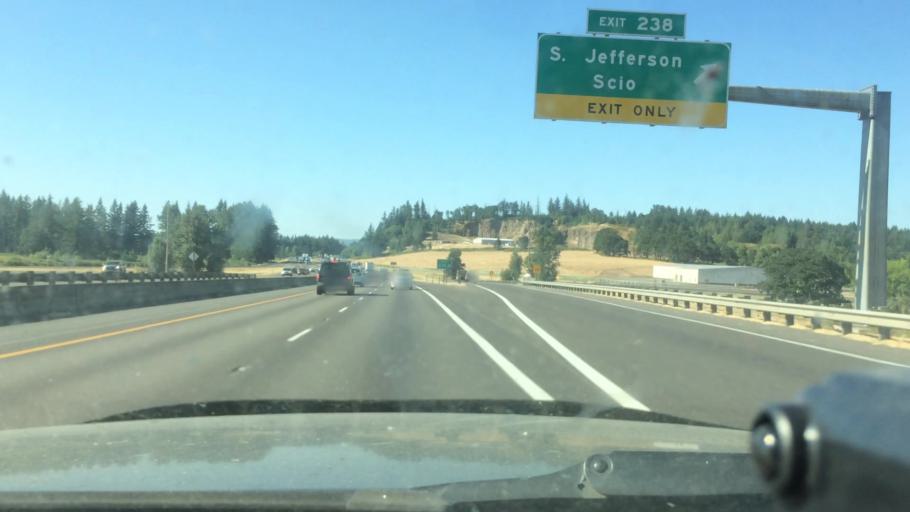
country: US
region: Oregon
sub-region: Linn County
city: Millersburg
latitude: 44.7025
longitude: -123.0520
